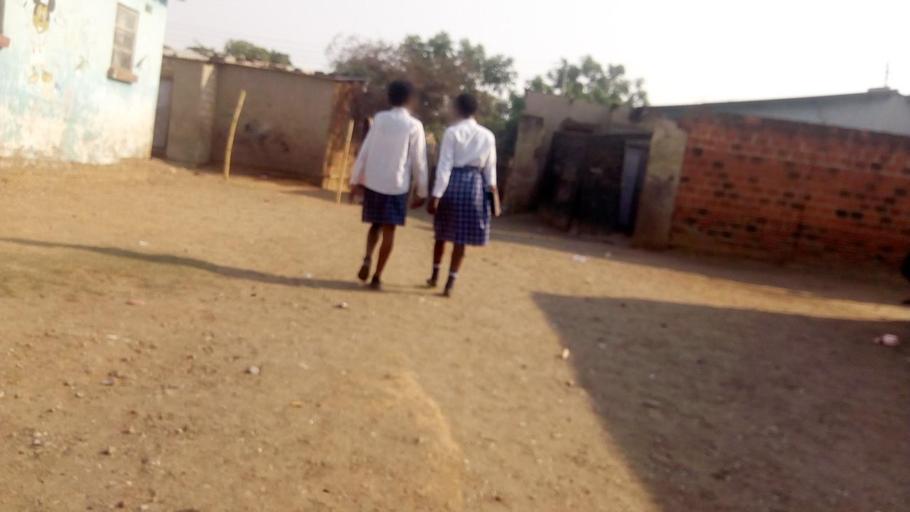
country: ZM
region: Lusaka
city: Lusaka
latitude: -15.3619
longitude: 28.2979
